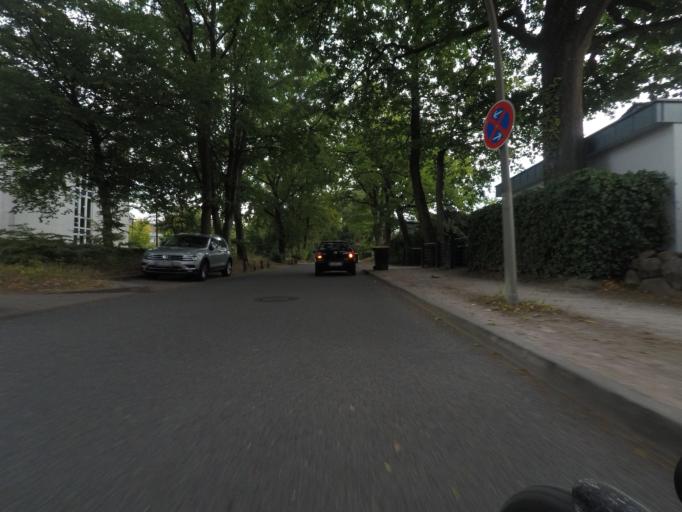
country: DE
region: Hamburg
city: Bergstedt
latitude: 53.6400
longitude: 10.1505
